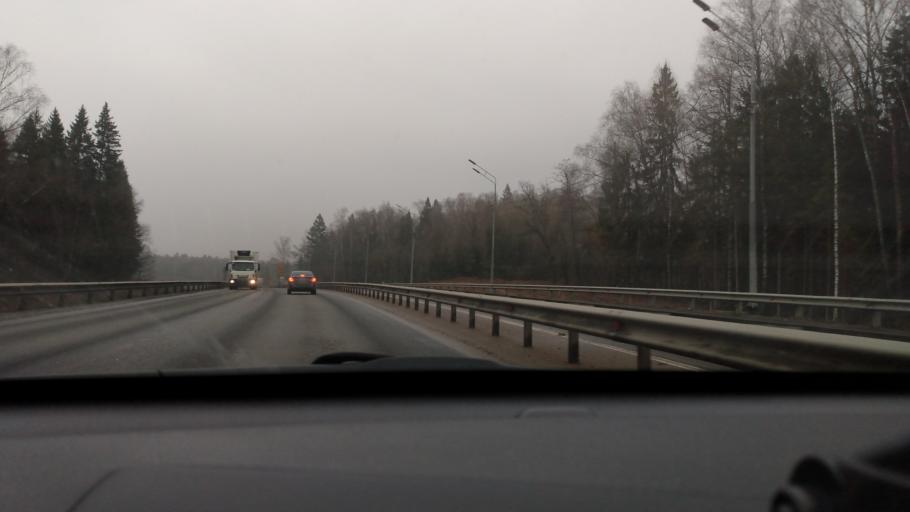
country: RU
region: Moskovskaya
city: Yershovo
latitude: 55.7882
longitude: 36.9204
